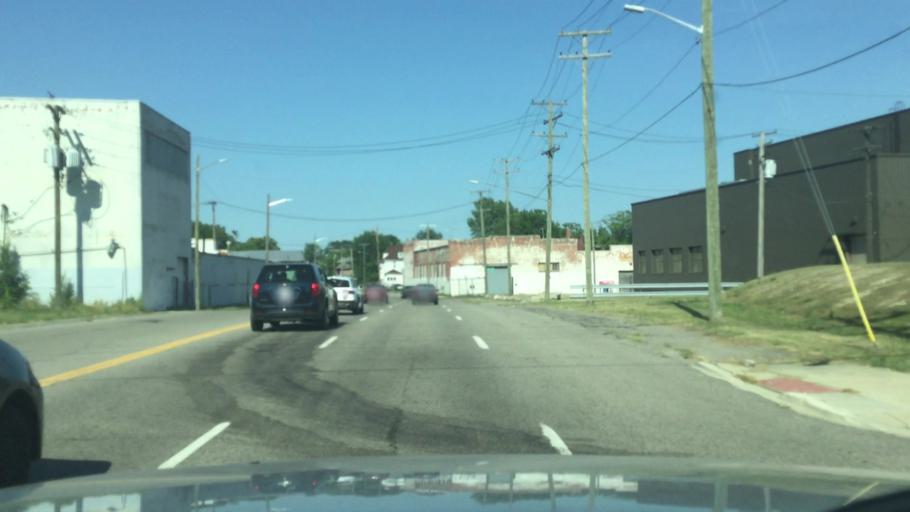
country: US
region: Michigan
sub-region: Wayne County
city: Detroit
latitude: 42.3558
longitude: -83.0146
